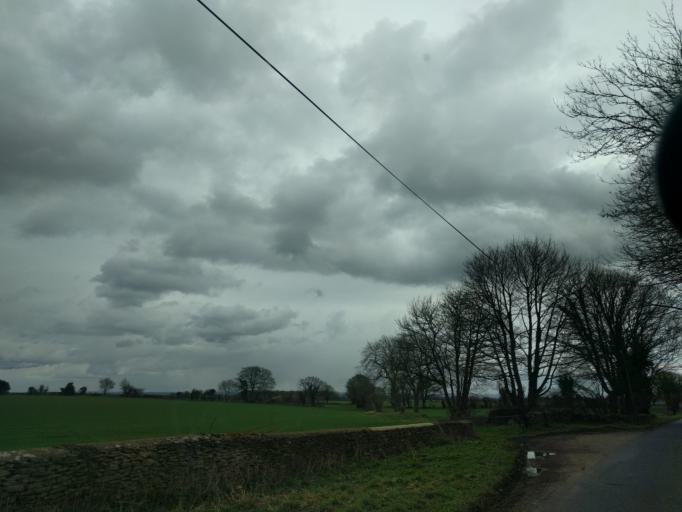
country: GB
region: England
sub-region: Gloucestershire
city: Nailsworth
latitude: 51.6458
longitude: -2.2497
